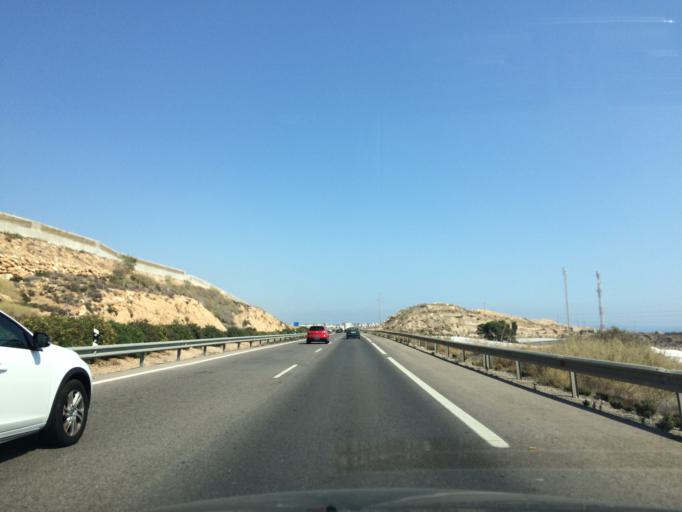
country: ES
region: Andalusia
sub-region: Provincia de Almeria
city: Vicar
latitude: 36.8125
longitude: -2.6198
